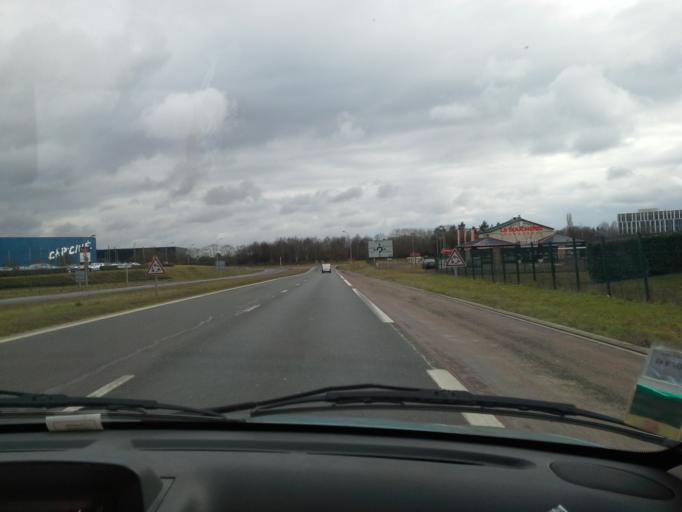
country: FR
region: Centre
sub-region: Departement du Loir-et-Cher
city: Villebarou
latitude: 47.6124
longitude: 1.3361
